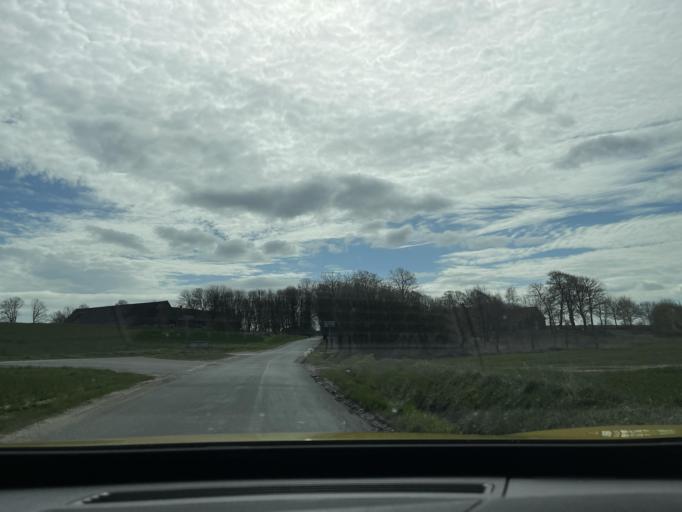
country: DK
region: Central Jutland
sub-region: Favrskov Kommune
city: Hinnerup
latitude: 56.3003
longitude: 10.1063
